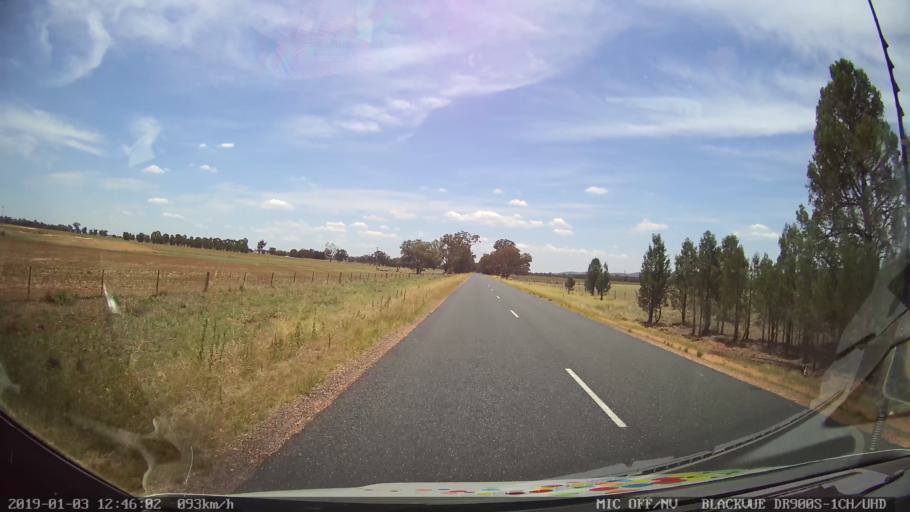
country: AU
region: New South Wales
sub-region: Weddin
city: Grenfell
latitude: -33.7424
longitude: 148.2286
